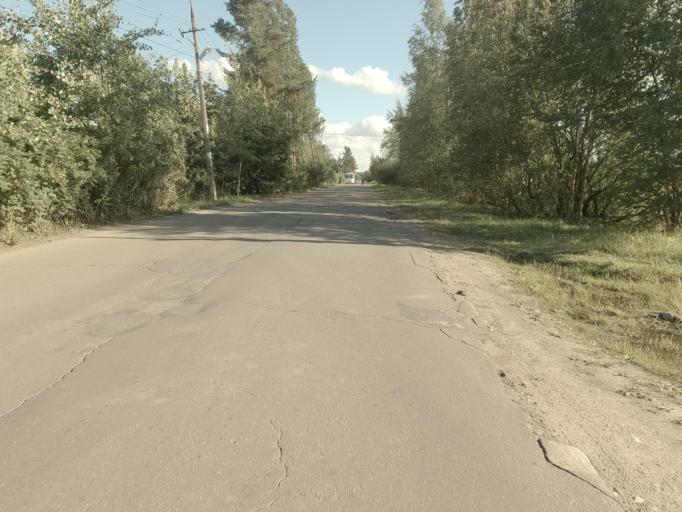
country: RU
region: Leningrad
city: Imeni Morozova
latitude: 59.9642
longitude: 31.0294
